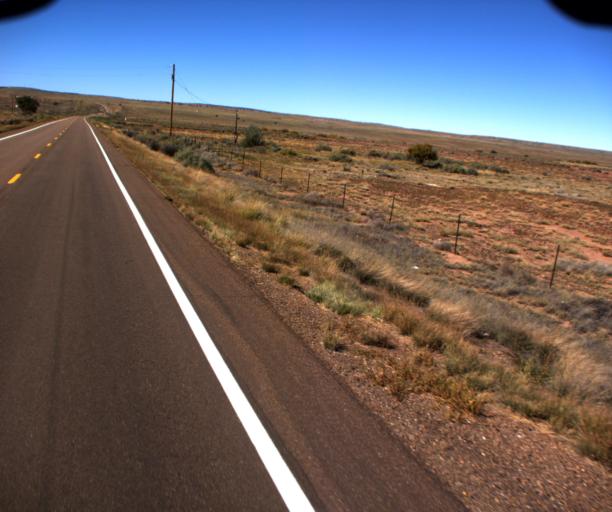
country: US
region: Arizona
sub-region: Apache County
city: Saint Johns
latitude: 34.5083
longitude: -109.4308
